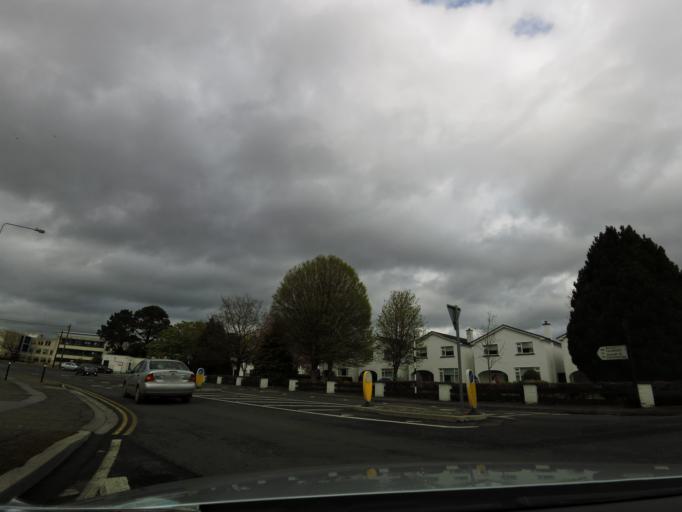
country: IE
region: Leinster
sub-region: Kilkenny
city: Kilkenny
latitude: 52.6641
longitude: -7.2629
